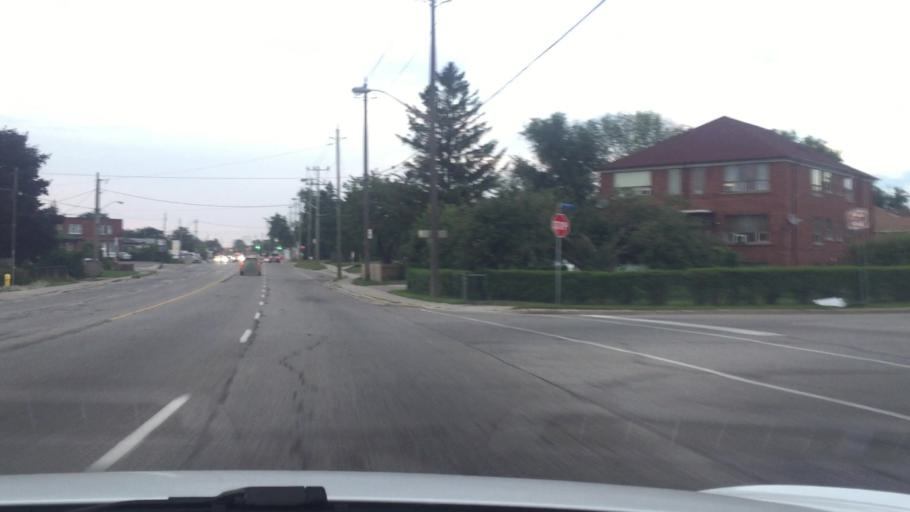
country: CA
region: Ontario
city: Scarborough
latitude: 43.7117
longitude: -79.2627
